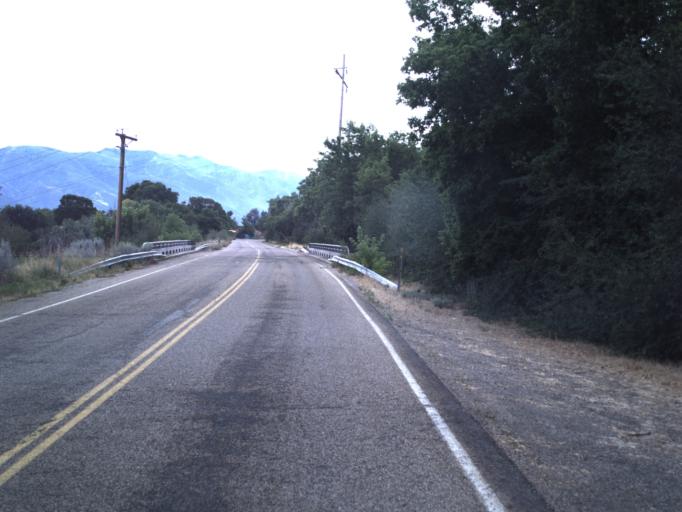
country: US
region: Utah
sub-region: Weber County
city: Riverdale
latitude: 41.1579
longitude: -112.0046
